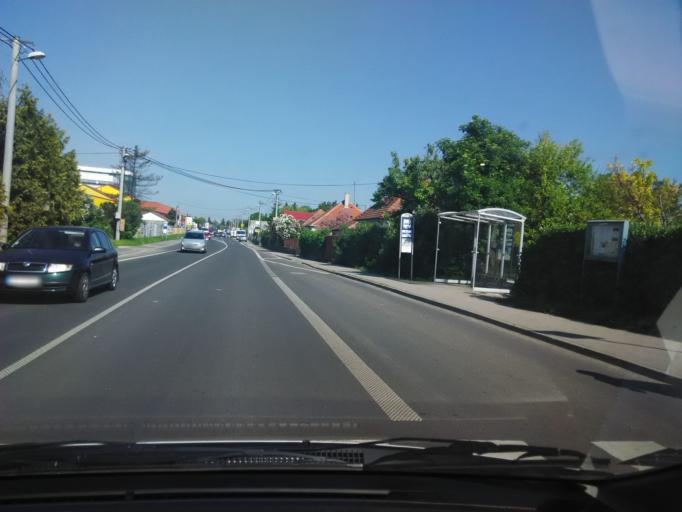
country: SK
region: Nitriansky
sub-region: Okres Nitra
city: Nitra
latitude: 48.2768
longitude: 18.0970
